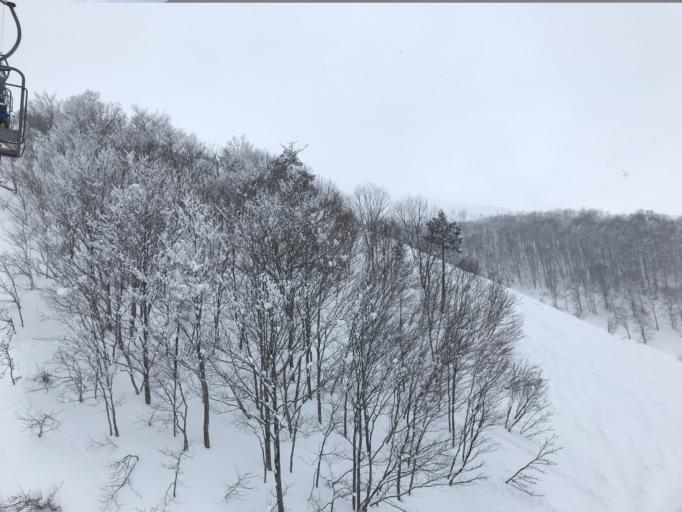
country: JP
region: Nagano
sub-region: Kitaazumi Gun
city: Hakuba
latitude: 36.7061
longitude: 137.8148
